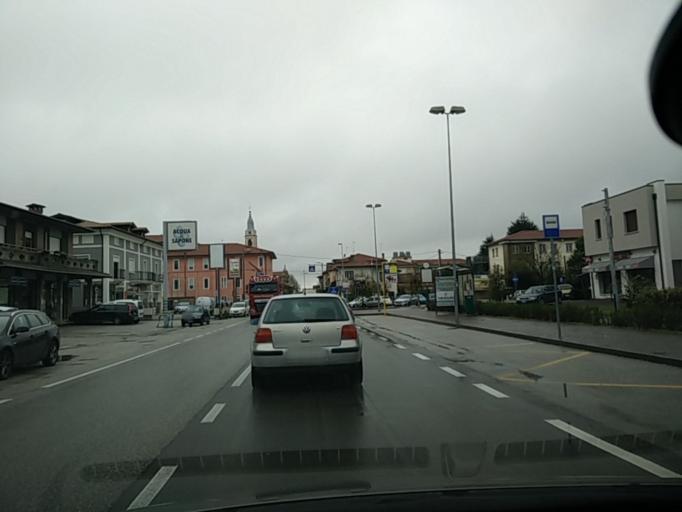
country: IT
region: Veneto
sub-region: Provincia di Vicenza
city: Rosa
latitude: 45.7272
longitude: 11.7620
